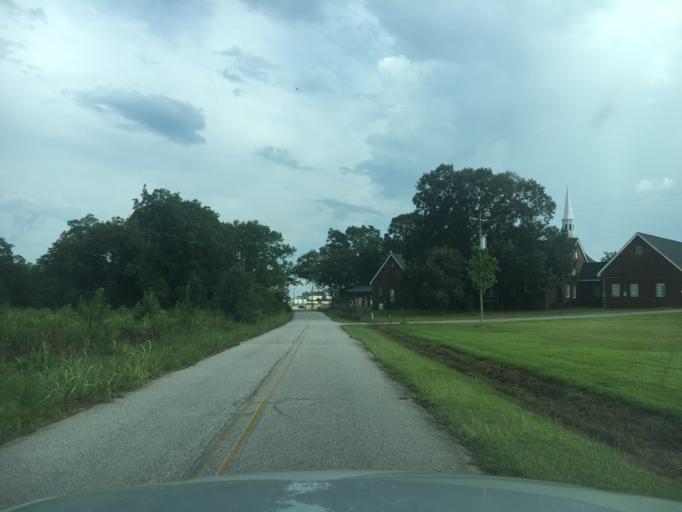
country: US
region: South Carolina
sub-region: Spartanburg County
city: Duncan
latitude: 34.9049
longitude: -82.1689
